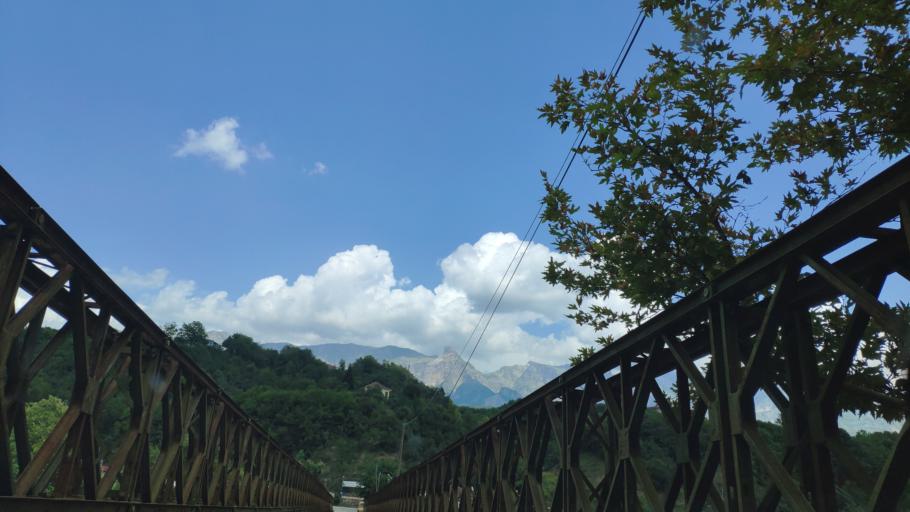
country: GR
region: Epirus
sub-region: Nomos Artas
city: Agios Dimitrios
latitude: 39.4546
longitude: 21.0328
